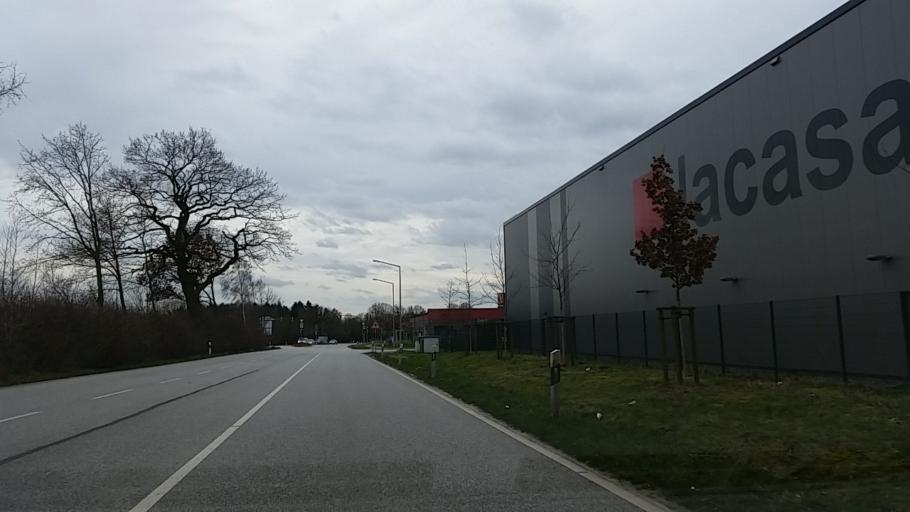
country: DE
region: Schleswig-Holstein
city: Braak
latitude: 53.6191
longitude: 10.2389
